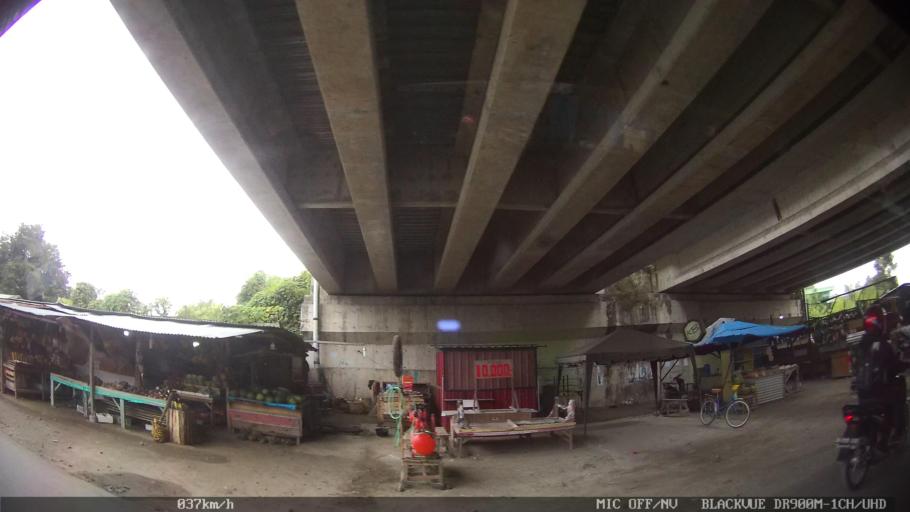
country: ID
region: North Sumatra
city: Sunggal
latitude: 3.6368
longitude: 98.5926
